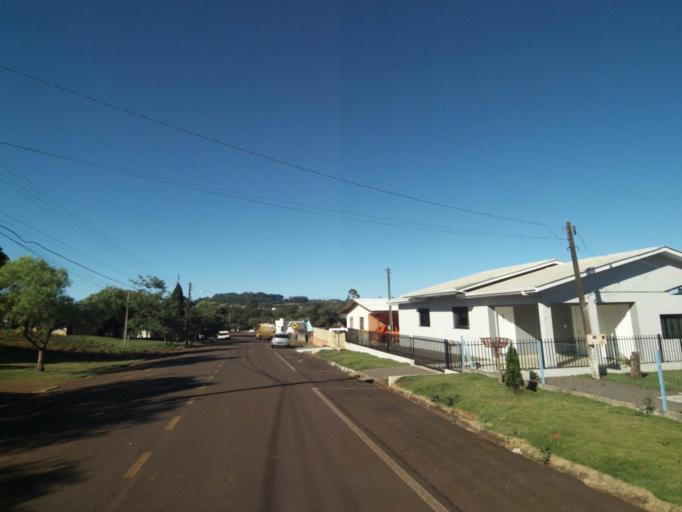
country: BR
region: Parana
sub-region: Pato Branco
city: Pato Branco
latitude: -26.2611
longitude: -52.7777
